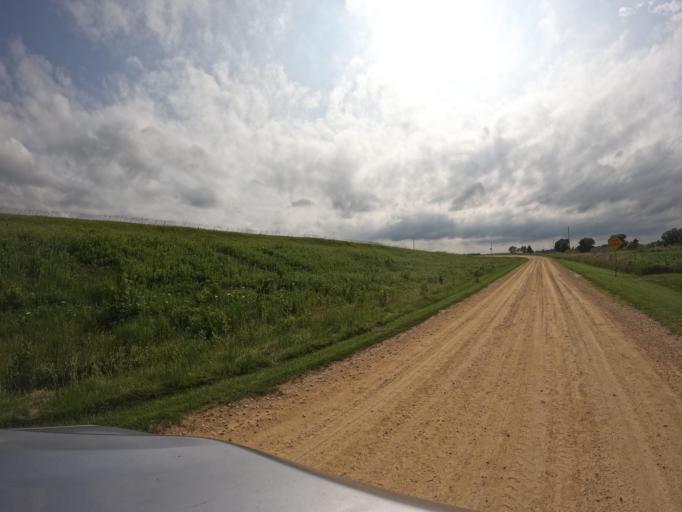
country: US
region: Iowa
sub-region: Clinton County
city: De Witt
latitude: 41.7858
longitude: -90.5690
